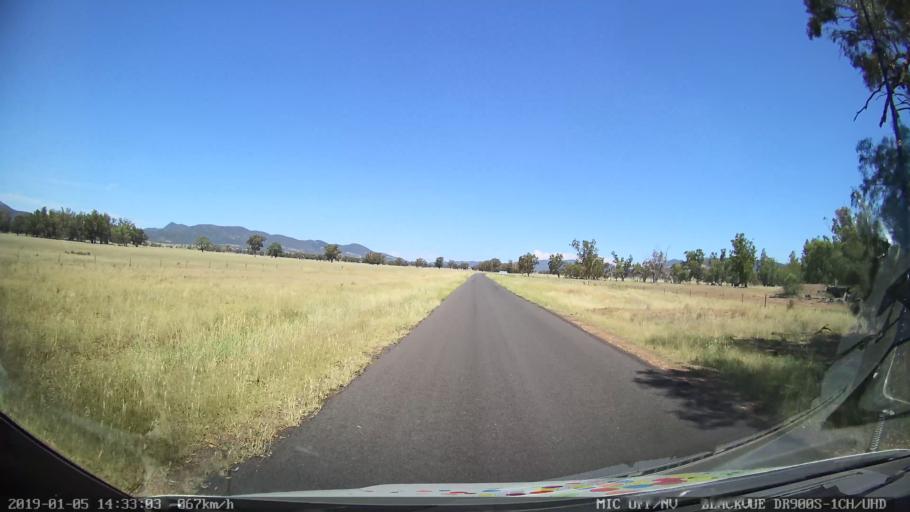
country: AU
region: New South Wales
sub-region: Tamworth Municipality
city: Phillip
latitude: -31.2234
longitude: 150.6253
